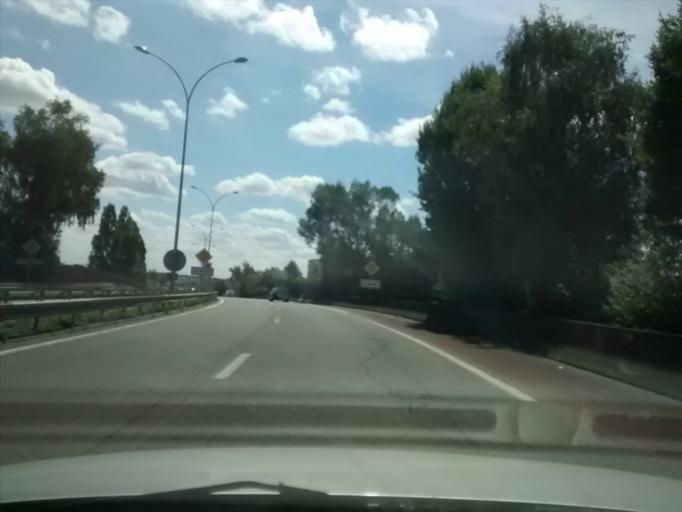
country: FR
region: Pays de la Loire
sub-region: Departement de la Sarthe
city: Le Mans
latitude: 47.9933
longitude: 0.1728
